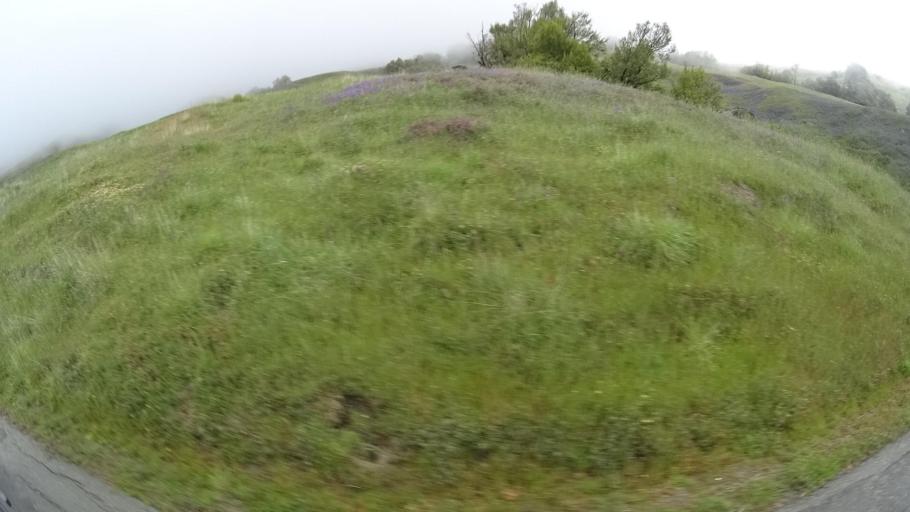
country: US
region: California
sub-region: Humboldt County
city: Redway
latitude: 40.1075
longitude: -123.6982
